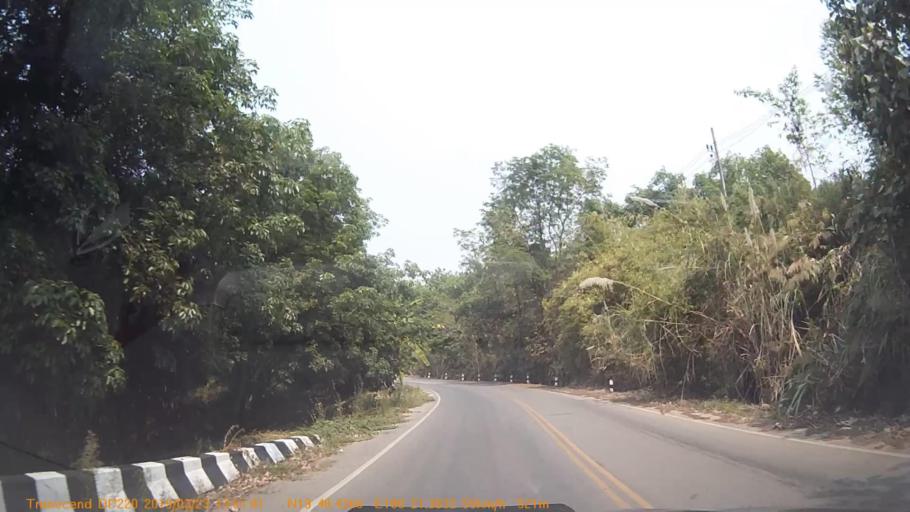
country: TH
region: Chiang Rai
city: Khun Tan
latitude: 19.8073
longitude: 100.3565
